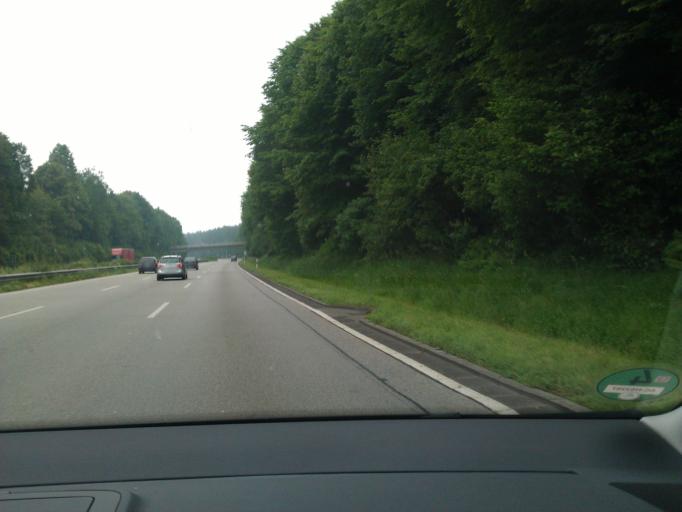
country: DE
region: Rheinland-Pfalz
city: Hundsdorf
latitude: 50.4495
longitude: 7.7087
